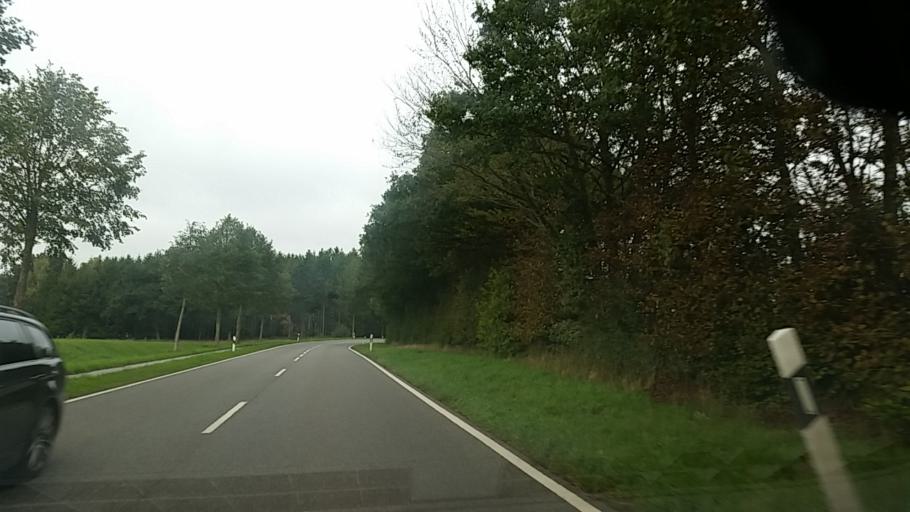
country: DE
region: Schleswig-Holstein
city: Hasenmoor
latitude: 53.8921
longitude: 9.9797
